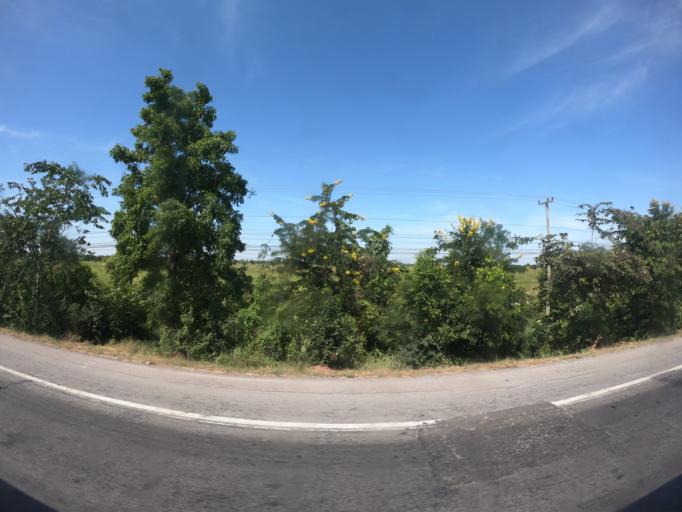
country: TH
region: Nakhon Ratchasima
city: Non Sung
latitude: 15.2136
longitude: 102.3580
